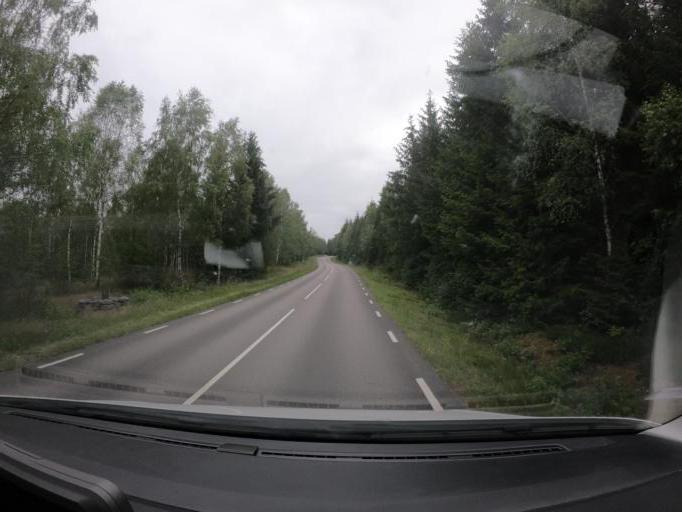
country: SE
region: Skane
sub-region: Perstorps Kommun
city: Perstorp
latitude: 56.0978
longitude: 13.4115
